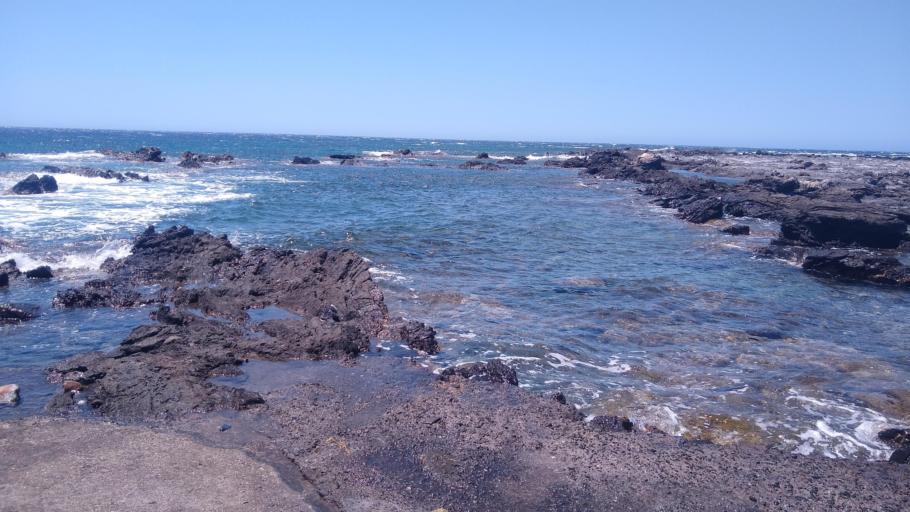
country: GR
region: Crete
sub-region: Nomos Chanias
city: Vryses
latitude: 35.3597
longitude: 23.5313
